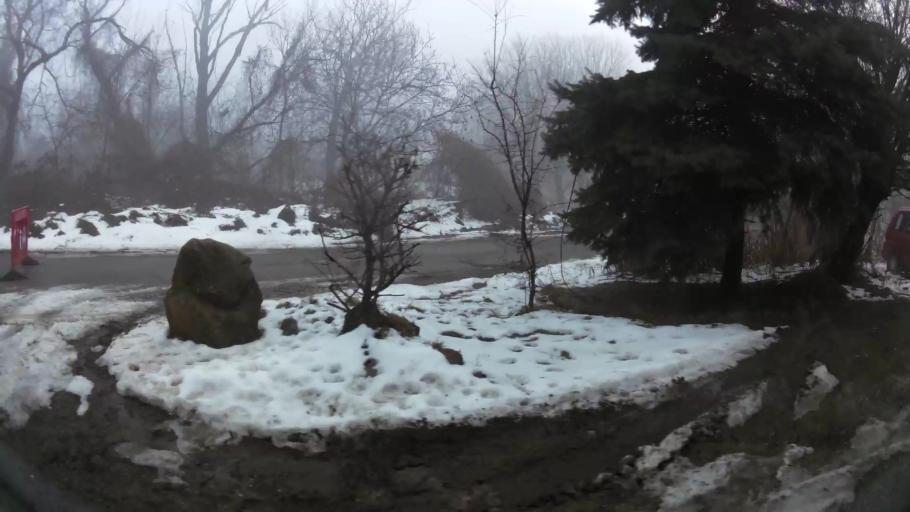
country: BG
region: Sofia-Capital
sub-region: Stolichna Obshtina
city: Sofia
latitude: 42.6569
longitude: 23.2529
